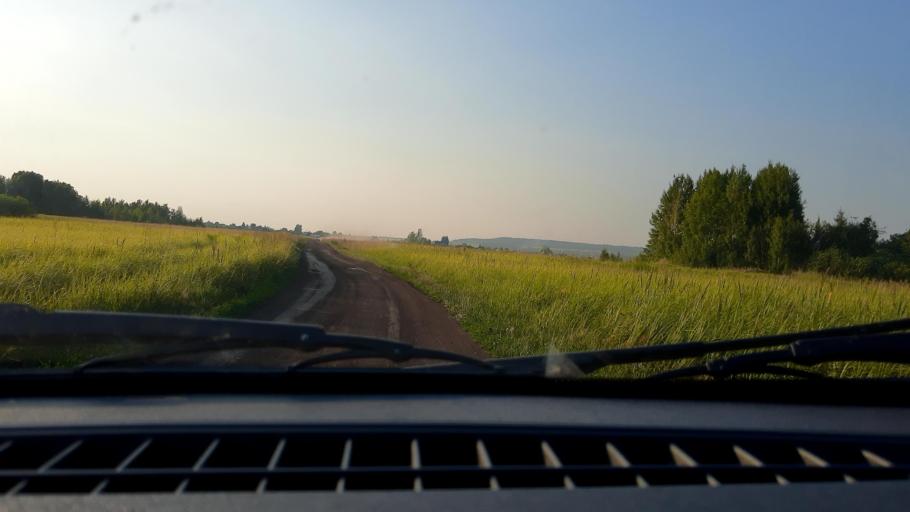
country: RU
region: Bashkortostan
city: Asanovo
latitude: 54.9386
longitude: 55.6220
